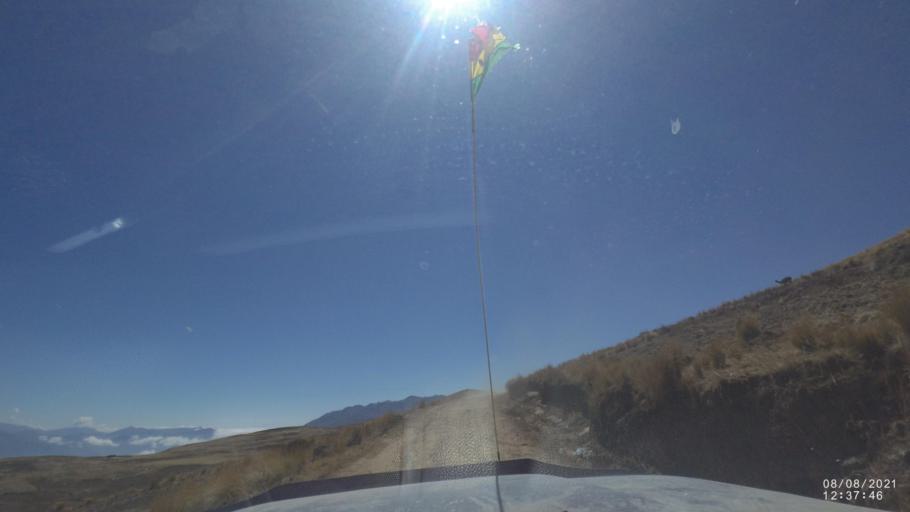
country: BO
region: Cochabamba
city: Colchani
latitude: -16.8362
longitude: -66.6265
